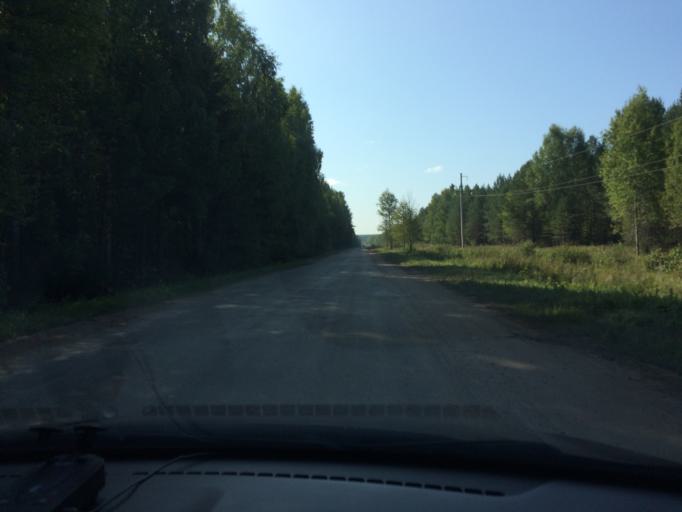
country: RU
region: Mariy-El
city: Sovetskiy
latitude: 56.5746
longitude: 48.4301
